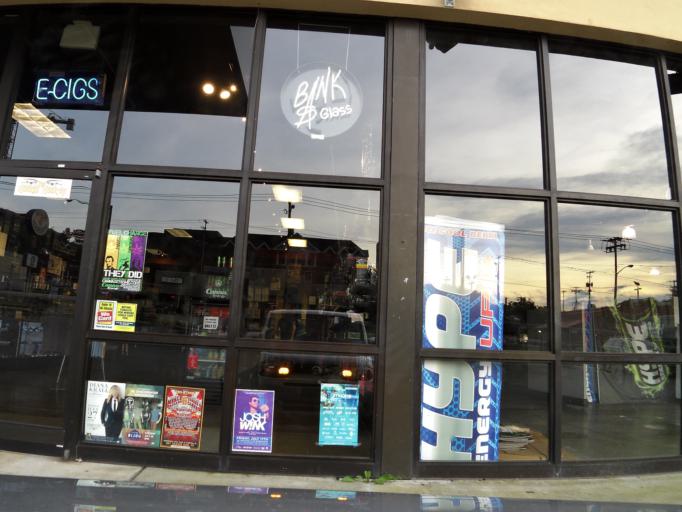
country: US
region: Tennessee
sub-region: Knox County
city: Knoxville
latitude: 35.9541
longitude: -83.9383
